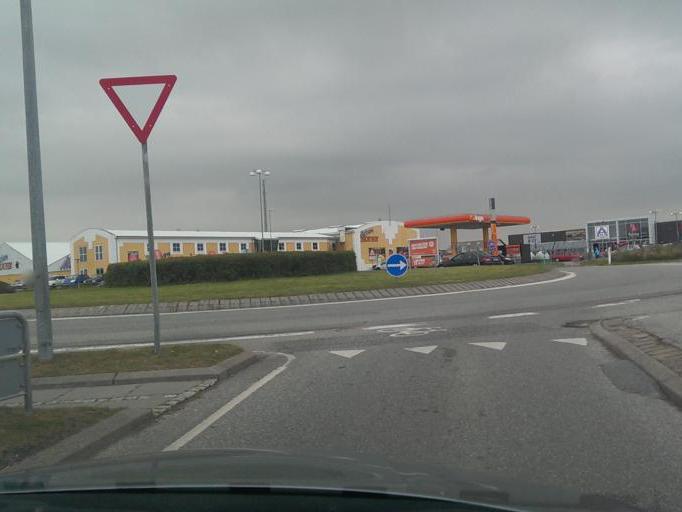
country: DK
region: North Denmark
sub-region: Jammerbugt Kommune
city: Pandrup
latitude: 57.3740
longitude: 9.7272
